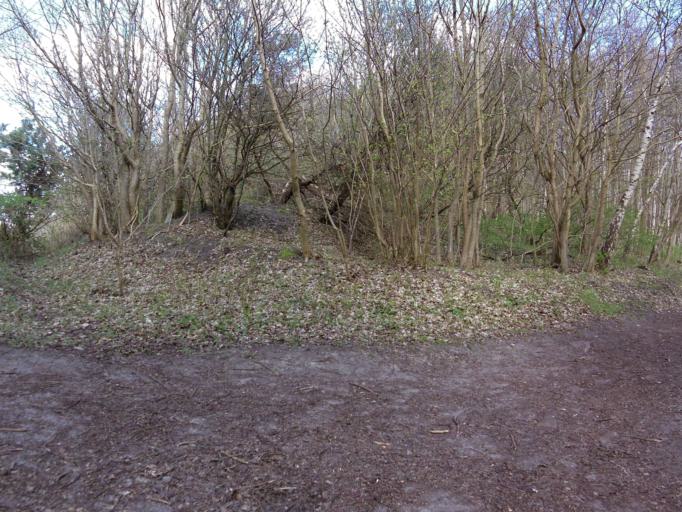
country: DE
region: Mecklenburg-Vorpommern
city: Hiddensee
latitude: 54.5921
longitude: 13.1035
